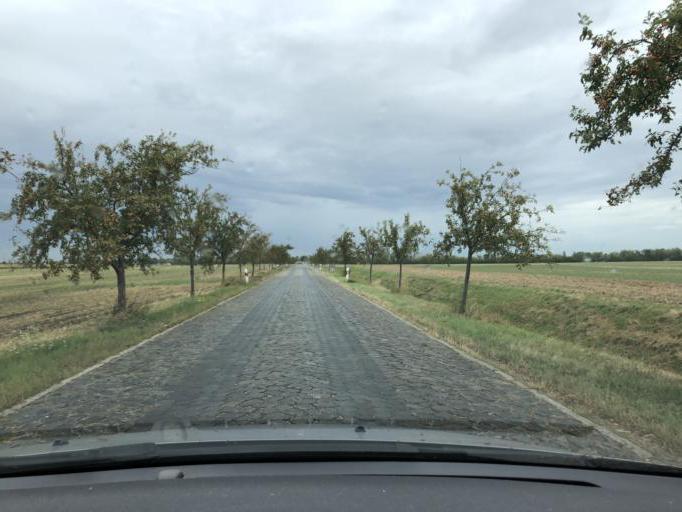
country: DE
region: Saxony-Anhalt
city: Wulfen
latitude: 51.8460
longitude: 11.8732
